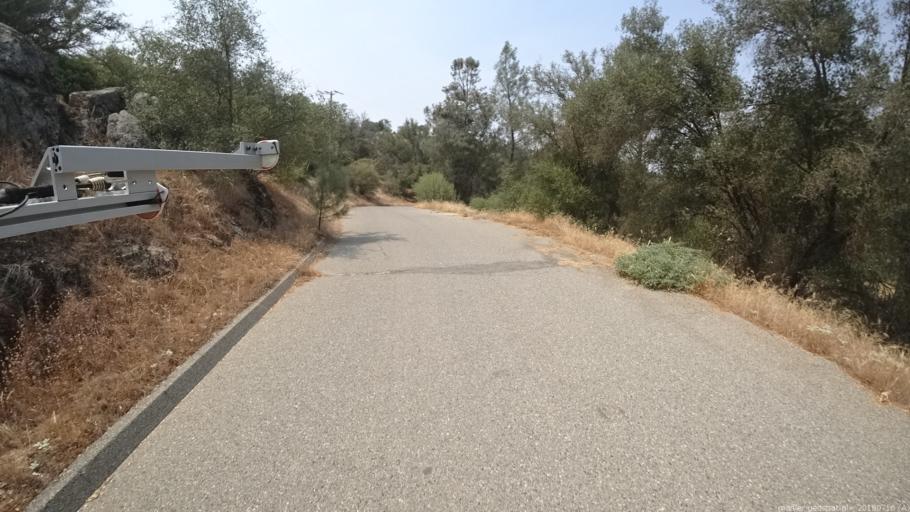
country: US
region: California
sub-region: Madera County
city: Yosemite Lakes
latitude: 37.2334
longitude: -119.7773
